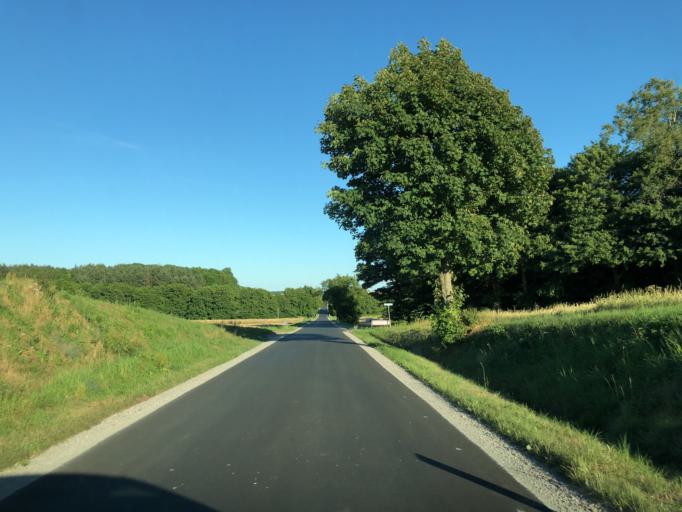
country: DK
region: Central Jutland
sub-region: Horsens Kommune
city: Horsens
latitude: 55.9515
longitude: 9.8475
